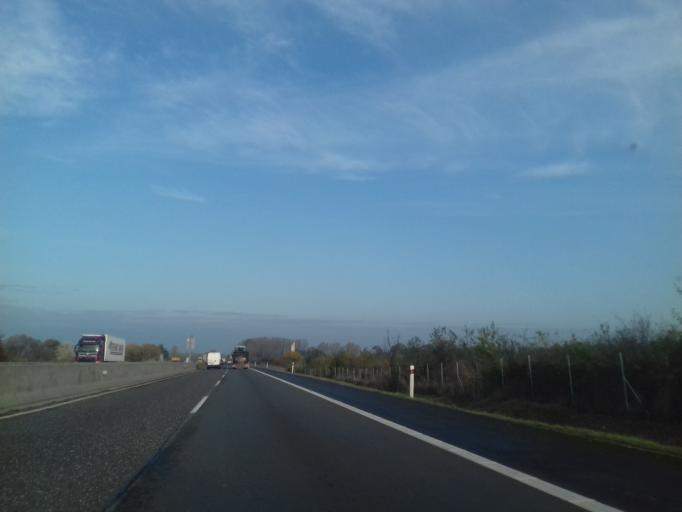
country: SK
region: Bratislavsky
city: Stupava
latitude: 48.2166
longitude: 17.0328
